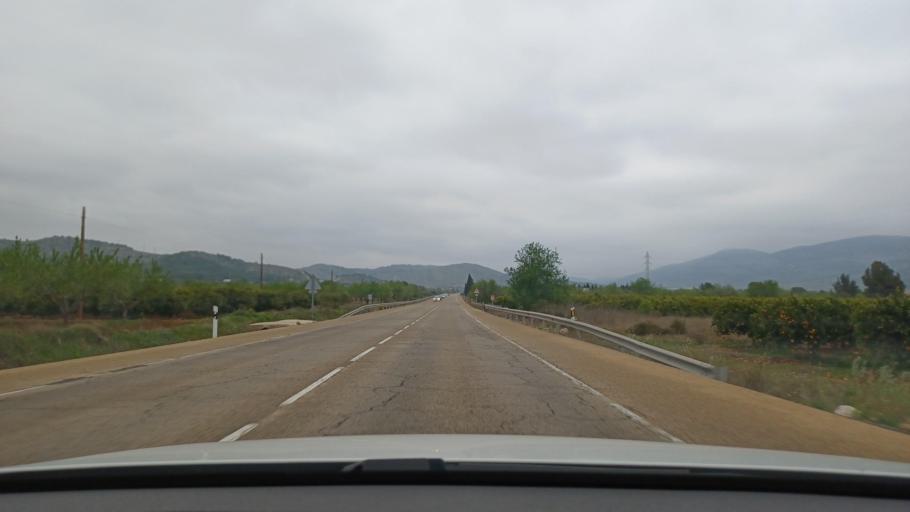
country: ES
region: Valencia
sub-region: Provincia de Castello
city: Torreblanca
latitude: 40.2489
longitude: 0.2335
